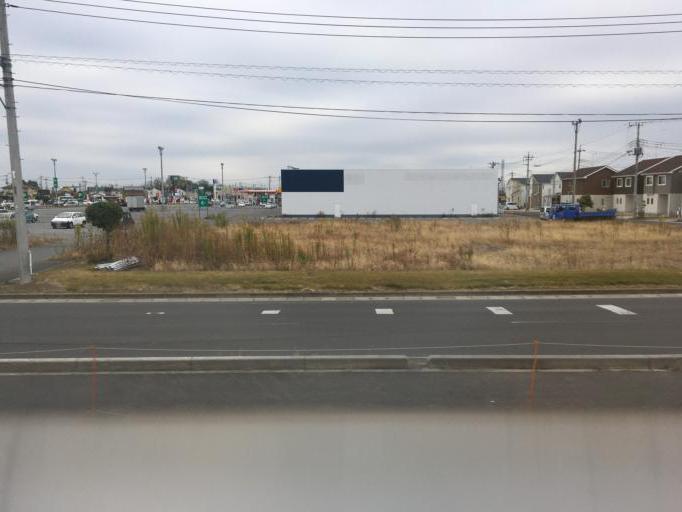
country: JP
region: Tochigi
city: Tochigi
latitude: 36.3531
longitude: 139.7078
